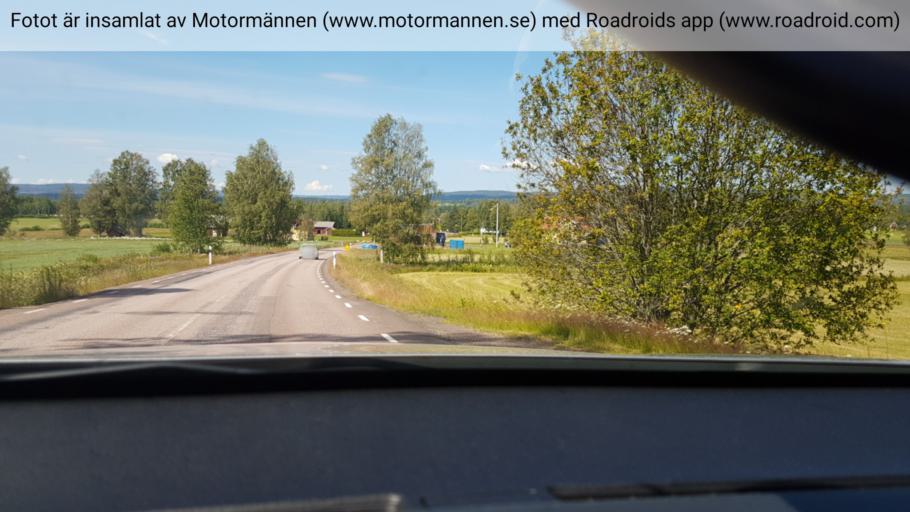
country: SE
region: Vaermland
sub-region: Sunne Kommun
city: Sunne
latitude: 59.8667
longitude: 13.2263
